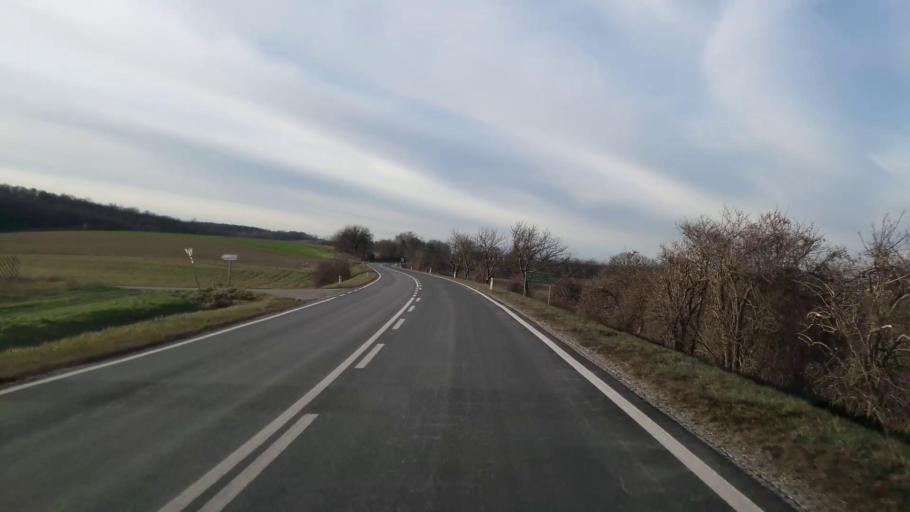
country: AT
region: Lower Austria
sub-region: Politischer Bezirk Ganserndorf
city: Gross-Schweinbarth
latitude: 48.4263
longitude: 16.6208
